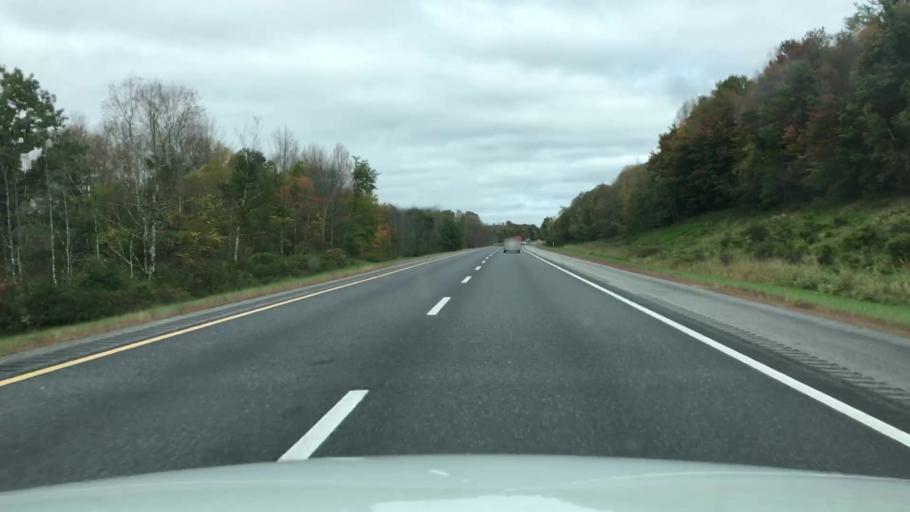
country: US
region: Maine
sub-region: Sagadahoc County
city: Richmond
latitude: 44.0710
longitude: -69.8787
